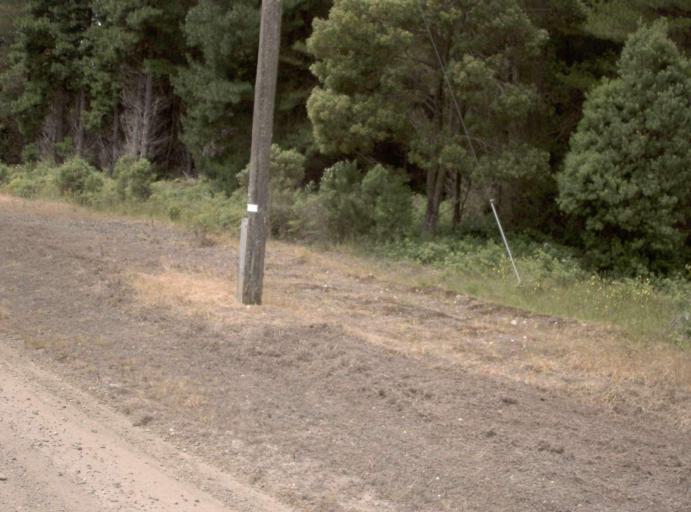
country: AU
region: Victoria
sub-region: Latrobe
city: Traralgon
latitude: -38.3965
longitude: 146.6577
